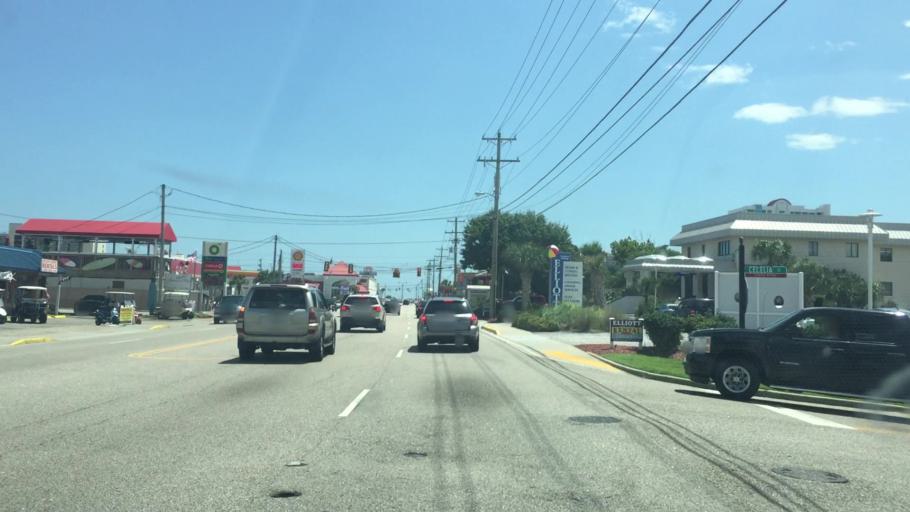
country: US
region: South Carolina
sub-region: Horry County
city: North Myrtle Beach
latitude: 33.8320
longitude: -78.6446
